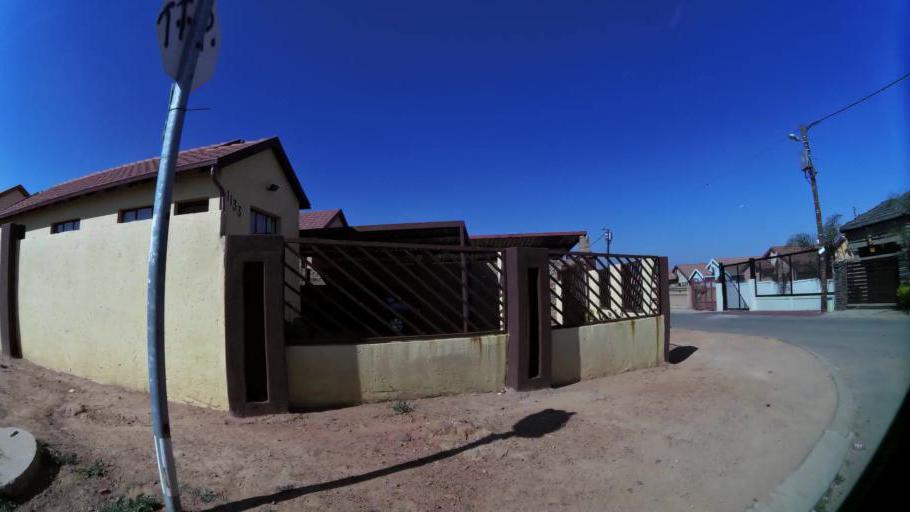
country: ZA
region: Gauteng
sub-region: City of Tshwane Metropolitan Municipality
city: Mabopane
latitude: -25.5611
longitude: 28.0770
